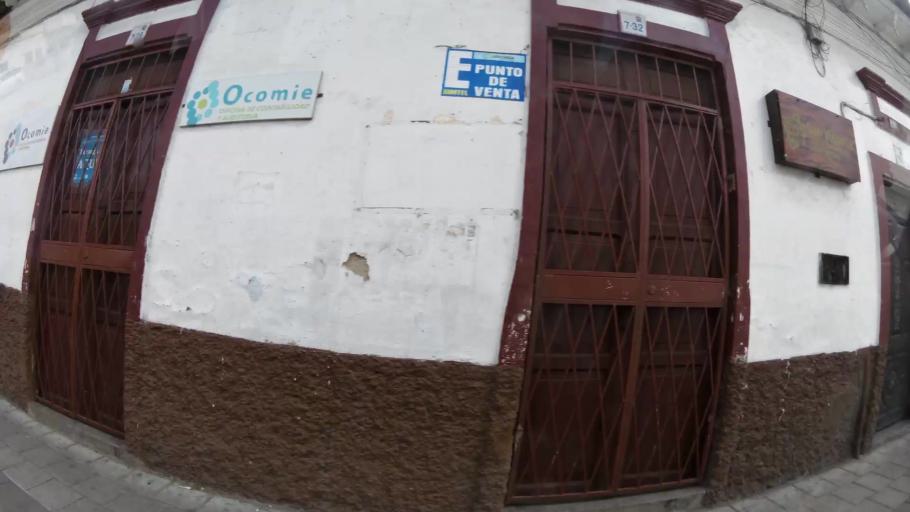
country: EC
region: Cotopaxi
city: Latacunga
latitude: -0.9307
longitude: -78.6146
